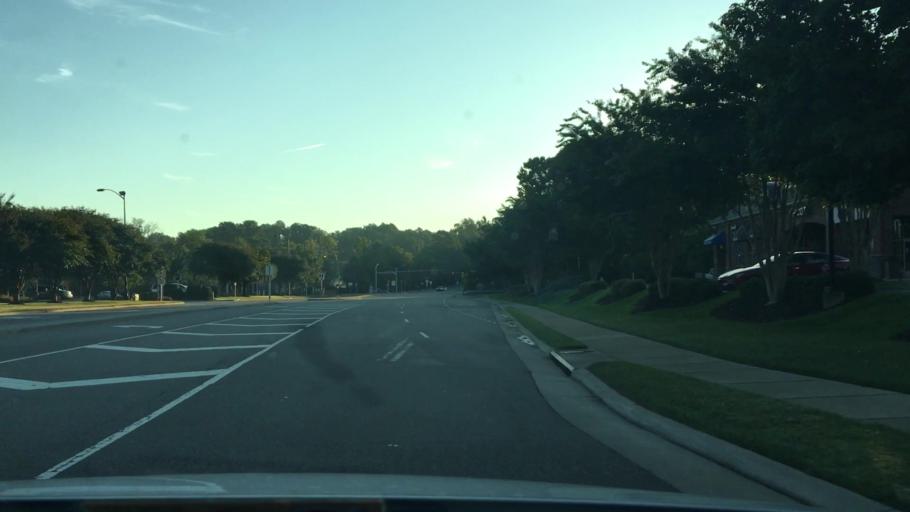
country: US
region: Virginia
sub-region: Henrico County
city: Tuckahoe
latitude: 37.5676
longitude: -77.5383
